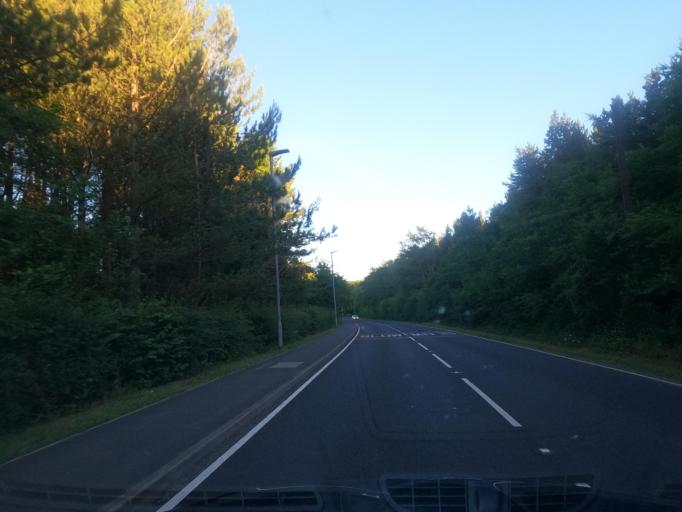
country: GB
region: England
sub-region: Northumberland
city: Seghill
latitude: 55.0786
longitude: -1.5484
